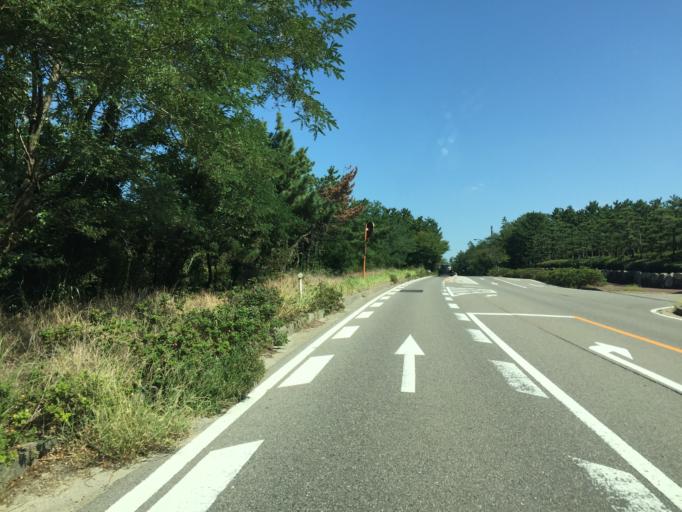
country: JP
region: Niigata
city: Niigata-shi
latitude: 37.9059
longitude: 138.9990
